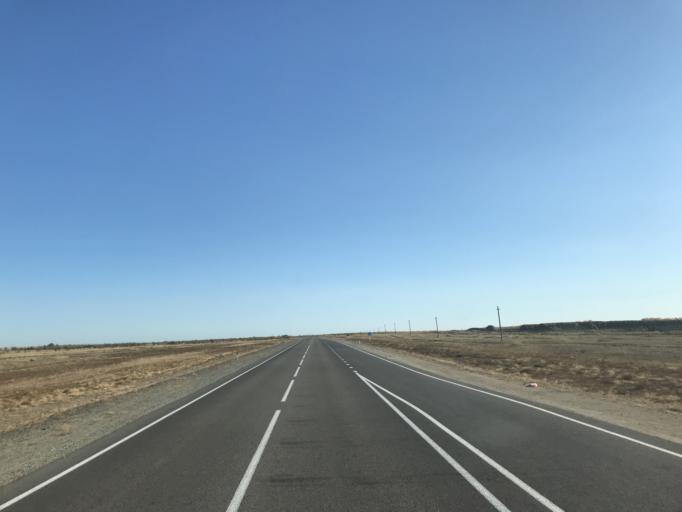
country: KZ
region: Pavlodar
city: Koktobe
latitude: 51.5369
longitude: 77.6482
